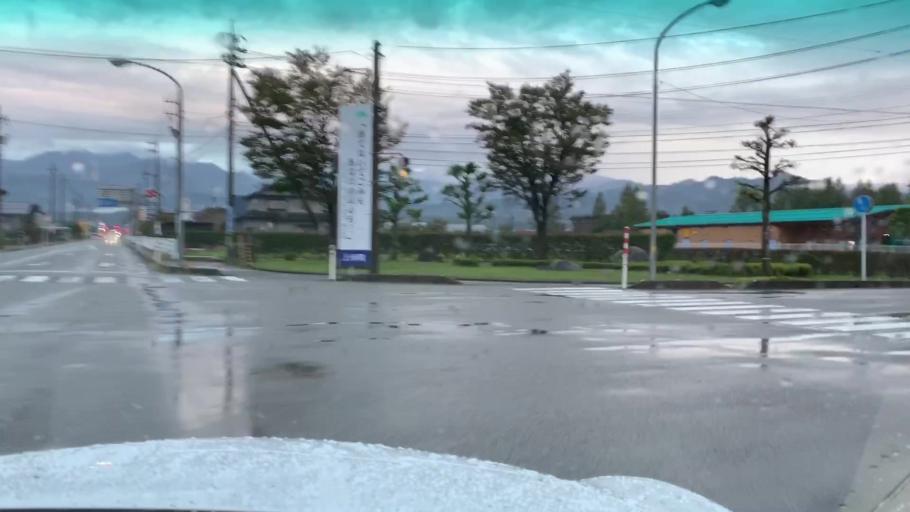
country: JP
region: Toyama
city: Kamiichi
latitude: 36.7003
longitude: 137.3423
